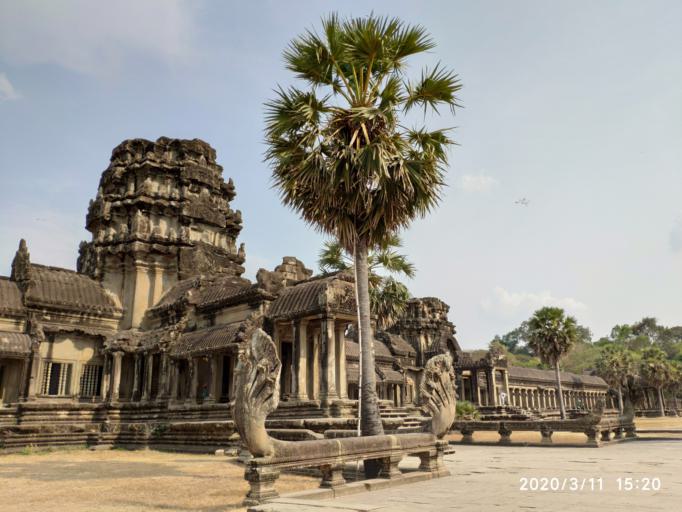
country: KH
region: Siem Reap
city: Siem Reap
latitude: 13.4127
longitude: 103.8615
